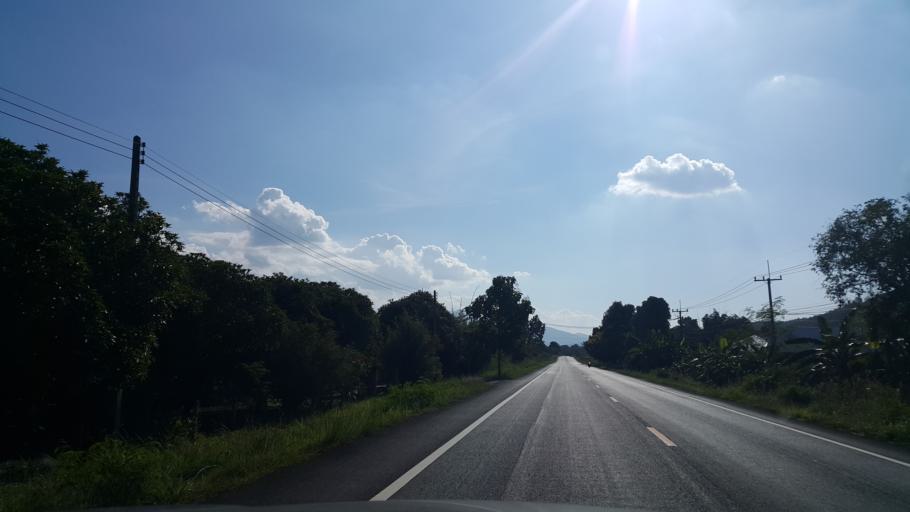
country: TH
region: Lamphun
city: Mae Tha
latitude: 18.4809
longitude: 99.1766
